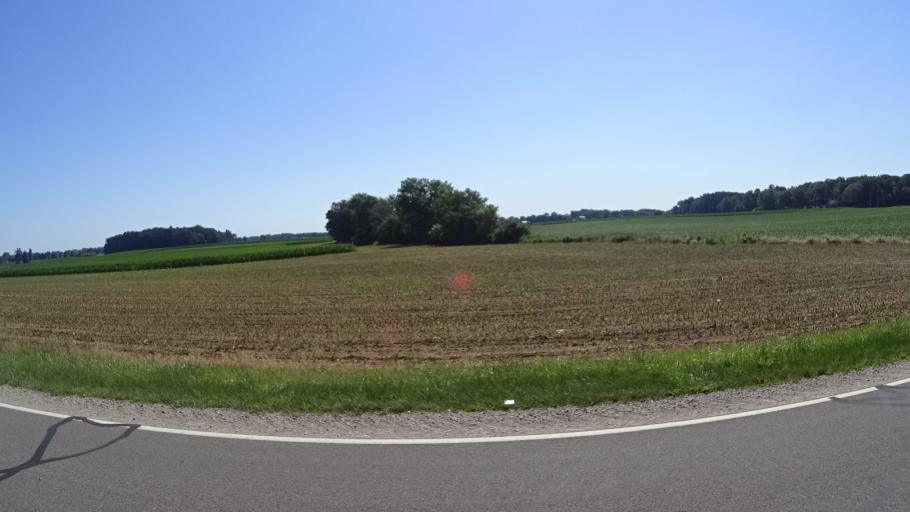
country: US
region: Ohio
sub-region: Erie County
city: Huron
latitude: 41.3795
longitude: -82.5904
